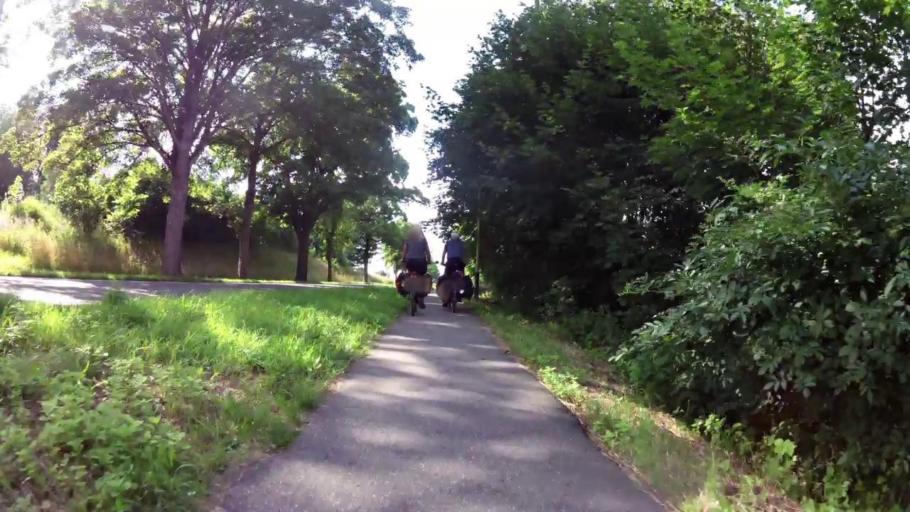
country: PL
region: West Pomeranian Voivodeship
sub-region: Powiat lobeski
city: Wegorzyno
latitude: 53.5484
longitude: 15.5461
